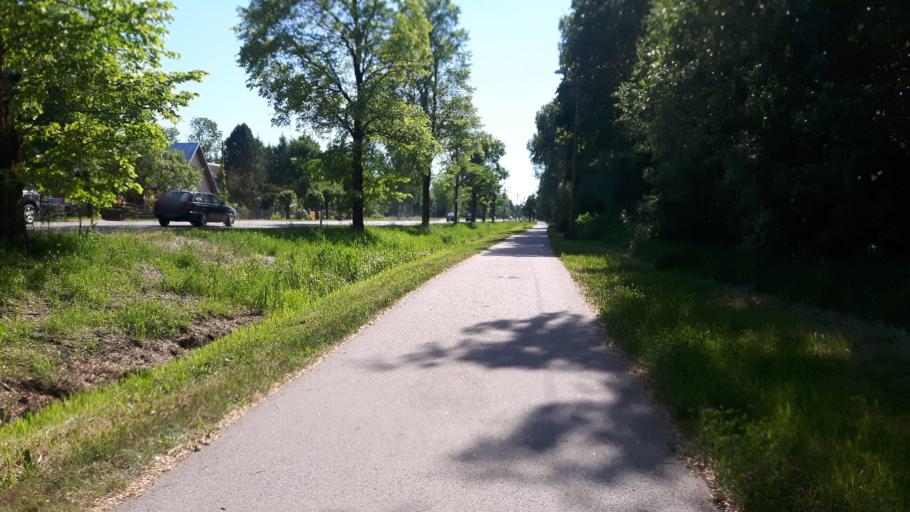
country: EE
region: Paernumaa
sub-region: Paikuse vald
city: Paikuse
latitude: 58.3819
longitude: 24.6329
